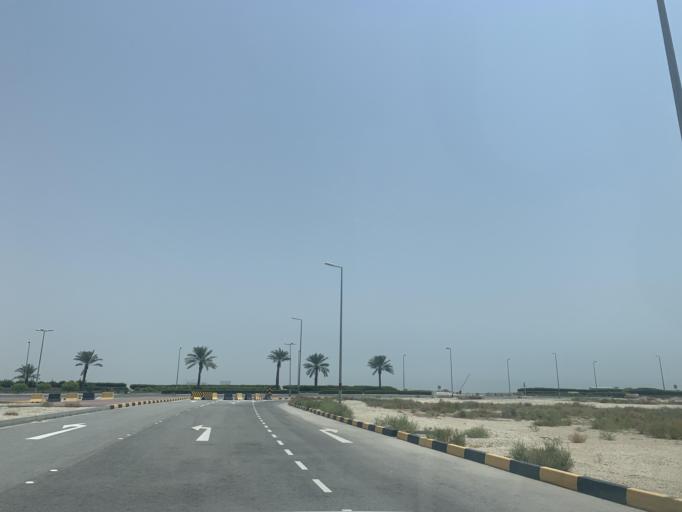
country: BH
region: Central Governorate
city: Dar Kulayb
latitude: 25.8478
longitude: 50.5917
